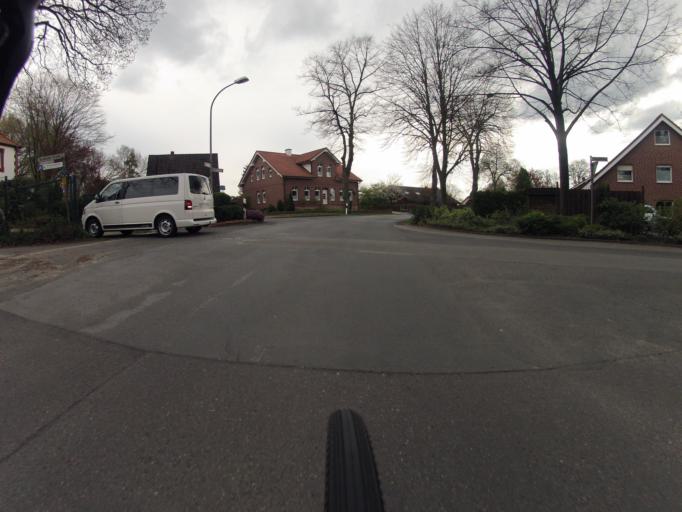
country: DE
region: North Rhine-Westphalia
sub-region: Regierungsbezirk Munster
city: Tecklenburg
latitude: 52.2584
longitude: 7.7832
